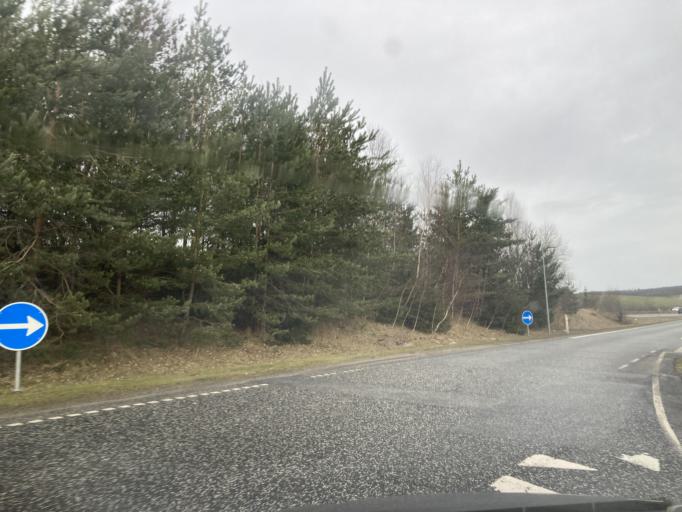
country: DK
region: North Denmark
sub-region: Rebild Kommune
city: Stovring
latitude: 56.8424
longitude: 9.7437
